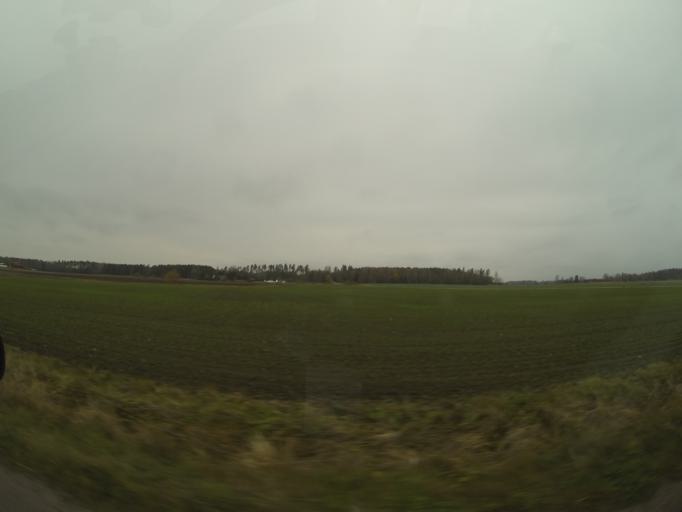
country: SE
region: Vaestmanland
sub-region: Kopings Kommun
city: Koping
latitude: 59.5576
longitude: 16.0967
